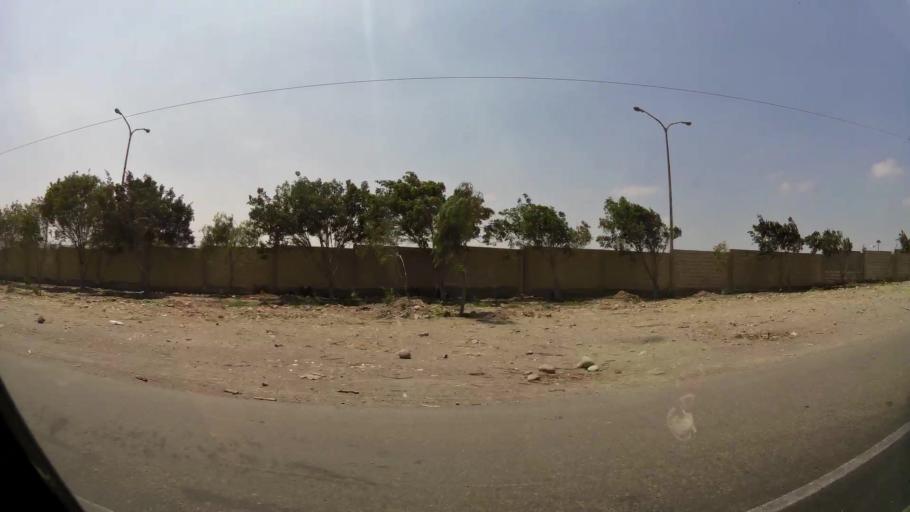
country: PE
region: La Libertad
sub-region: Provincia de Pacasmayo
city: Pacasmayo
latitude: -7.4051
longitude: -79.5570
